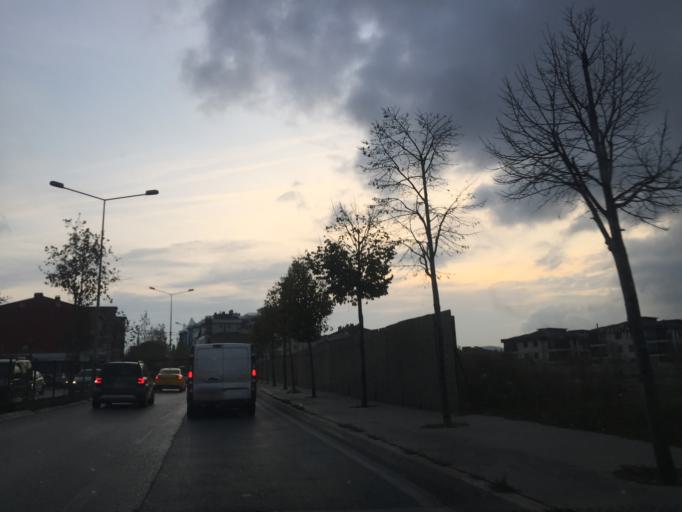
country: TR
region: Istanbul
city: Samandira
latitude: 40.9860
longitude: 29.2235
